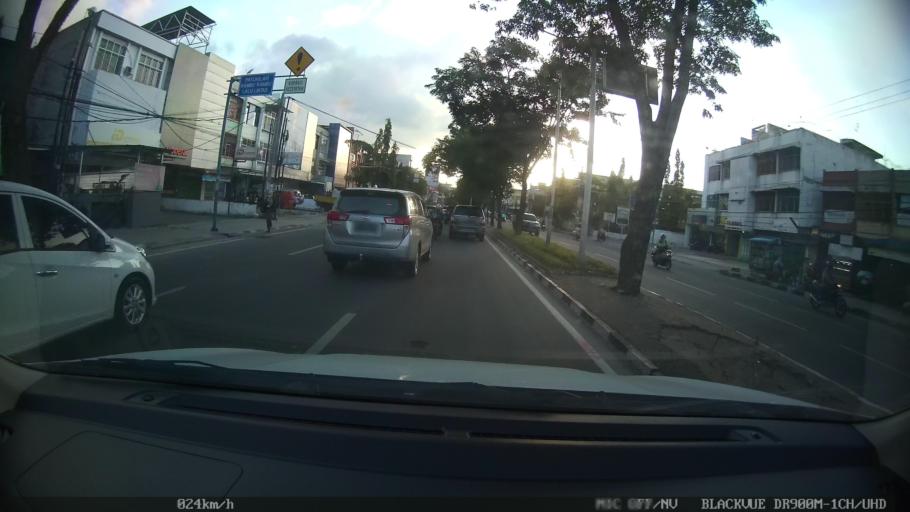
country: ID
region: North Sumatra
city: Medan
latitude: 3.5906
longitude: 98.6612
